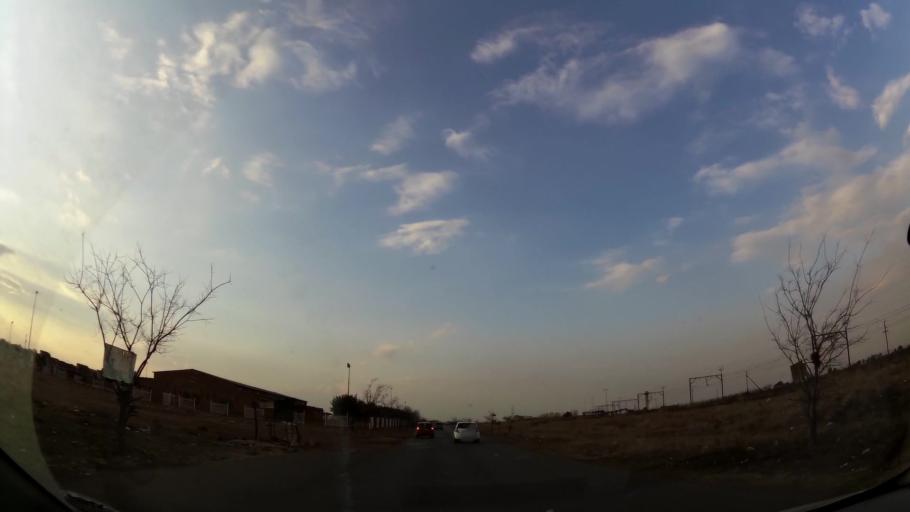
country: ZA
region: Gauteng
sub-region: City of Johannesburg Metropolitan Municipality
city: Orange Farm
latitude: -26.5680
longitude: 27.8613
